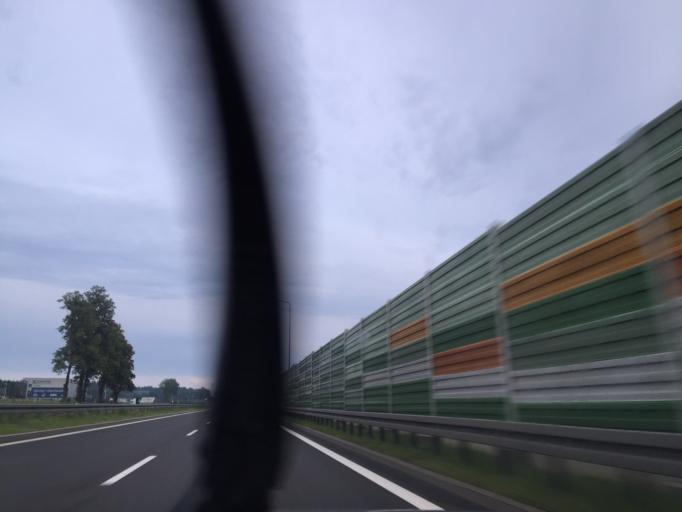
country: PL
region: Podlasie
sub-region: Powiat bialostocki
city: Choroszcz
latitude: 53.1528
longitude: 23.0347
